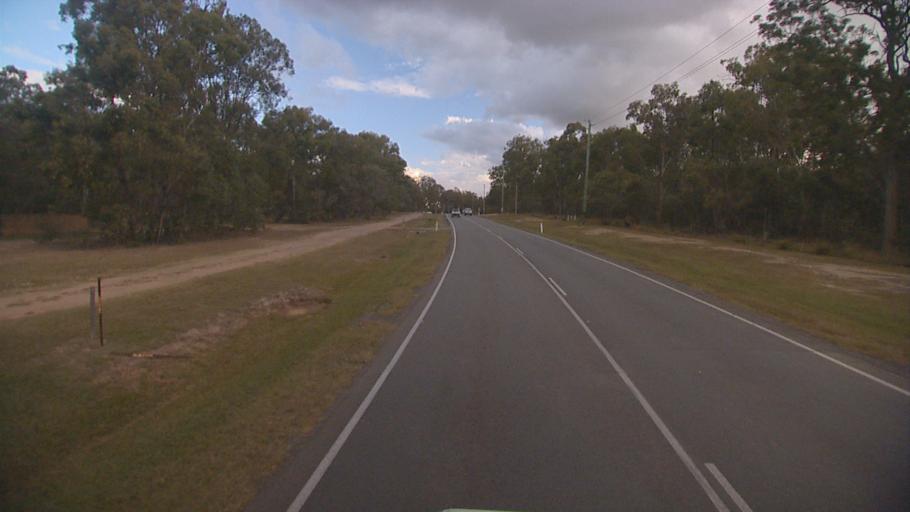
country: AU
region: Queensland
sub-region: Logan
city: Park Ridge South
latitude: -27.7137
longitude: 152.9944
